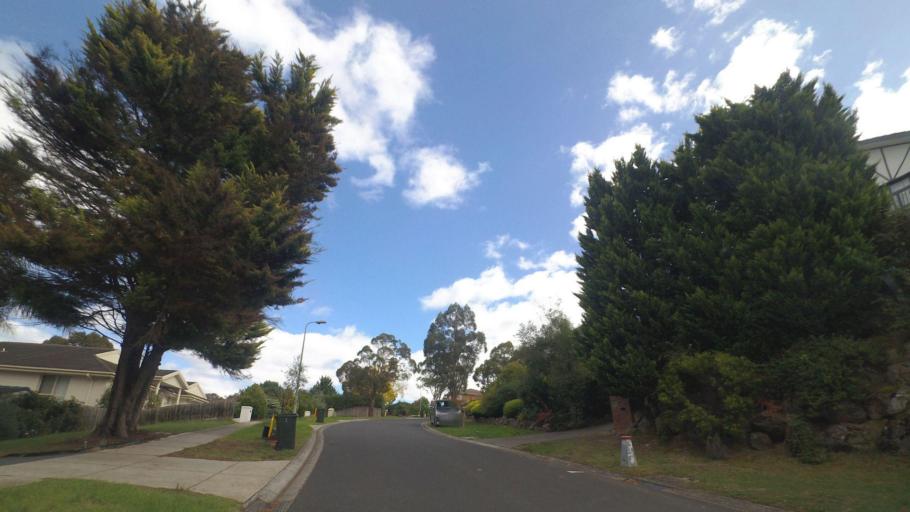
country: AU
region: Victoria
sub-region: Manningham
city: Donvale
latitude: -37.7643
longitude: 145.1783
